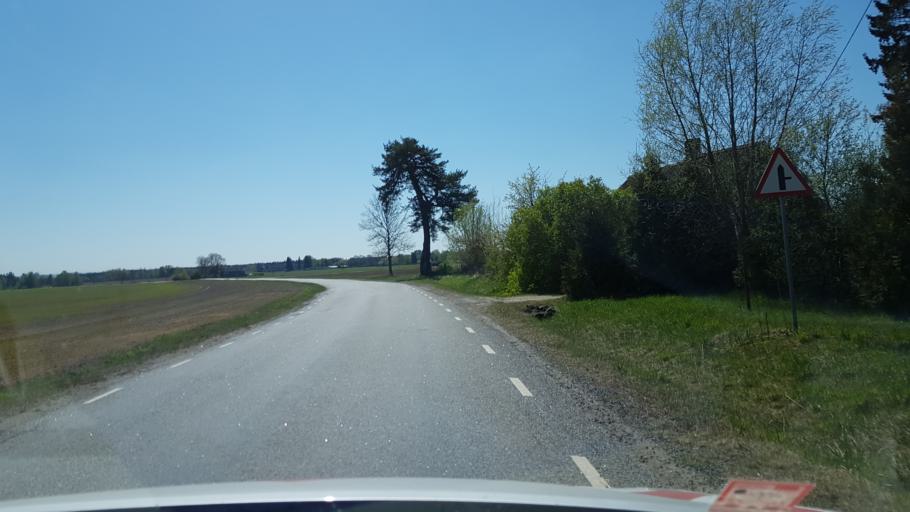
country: EE
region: Vorumaa
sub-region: Voru linn
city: Voru
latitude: 57.9237
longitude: 26.9510
